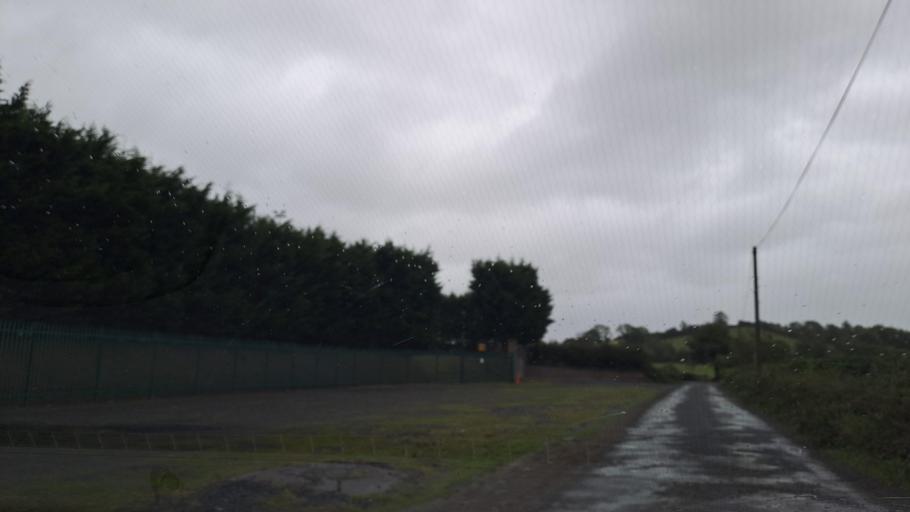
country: IE
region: Ulster
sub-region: An Cabhan
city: Kingscourt
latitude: 54.0081
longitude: -6.8233
